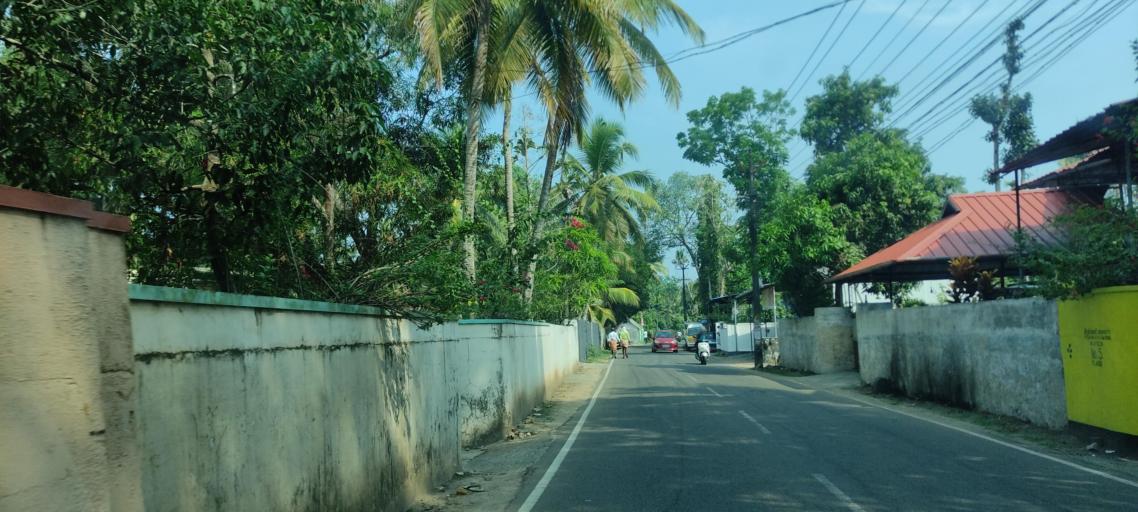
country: IN
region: Kerala
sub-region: Alappuzha
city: Kutiatodu
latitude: 9.8010
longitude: 76.3012
